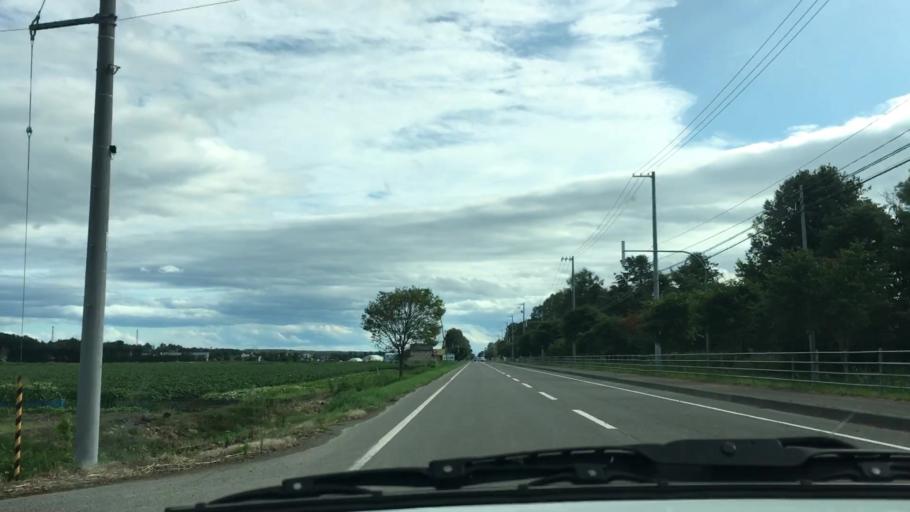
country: JP
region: Hokkaido
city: Otofuke
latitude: 43.2472
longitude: 143.2984
